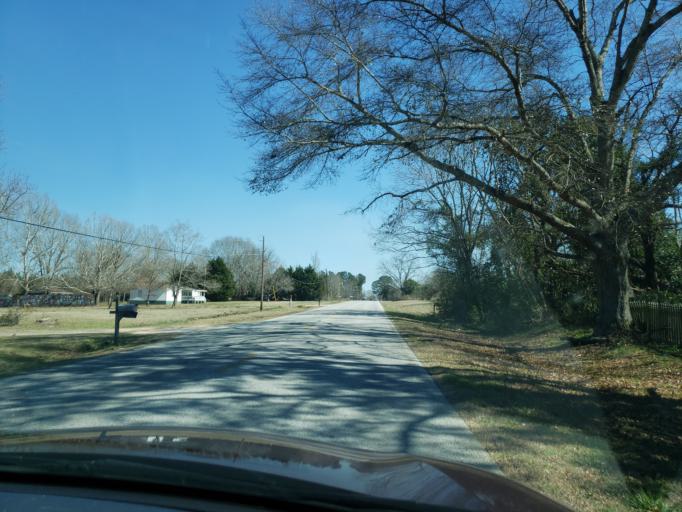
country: US
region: Alabama
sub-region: Elmore County
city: Tallassee
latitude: 32.5814
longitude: -85.7553
